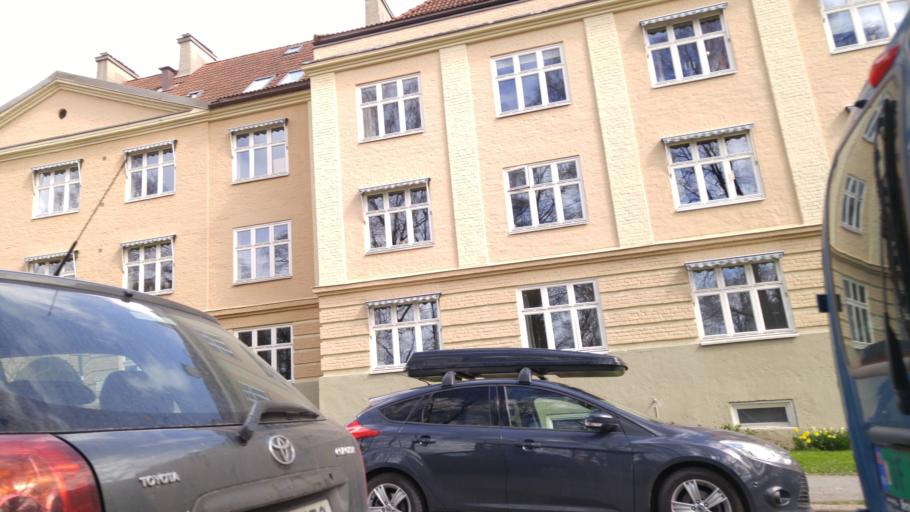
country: NO
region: Oslo
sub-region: Oslo
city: Oslo
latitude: 59.9355
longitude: 10.7728
